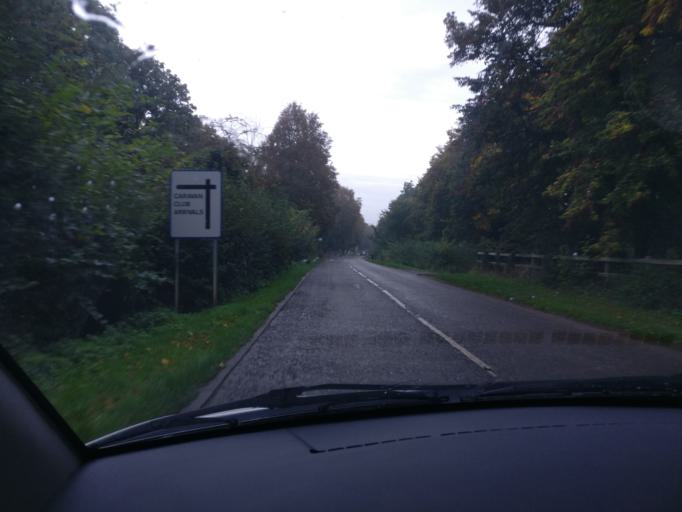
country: GB
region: England
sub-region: Peterborough
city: Castor
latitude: 52.5598
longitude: -0.3048
